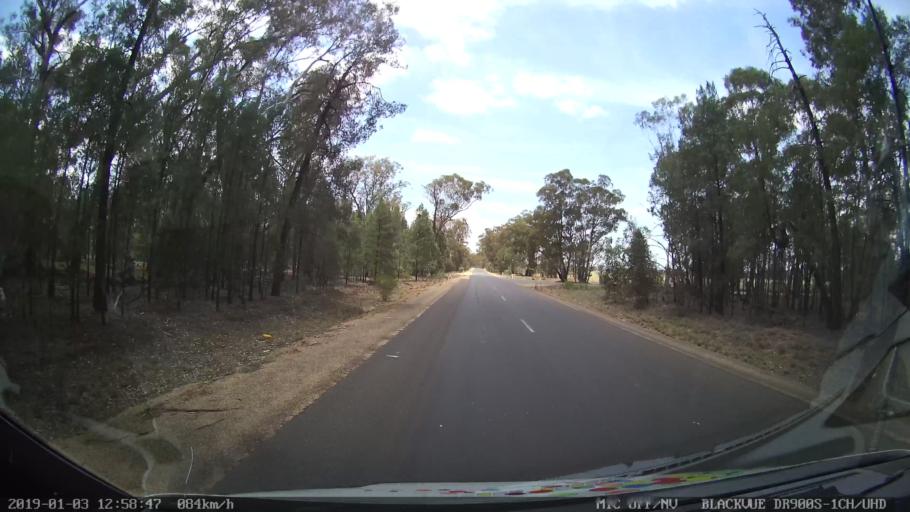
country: AU
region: New South Wales
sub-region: Cabonne
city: Canowindra
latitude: -33.6403
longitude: 148.3802
